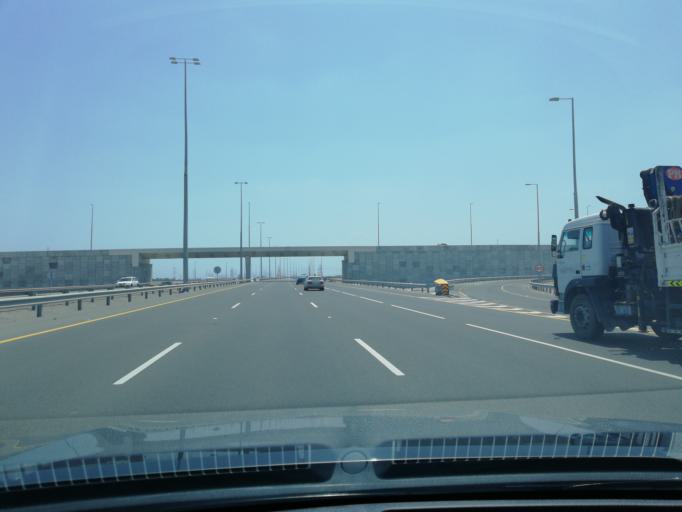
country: OM
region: Al Batinah
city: Barka'
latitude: 23.6313
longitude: 57.9882
